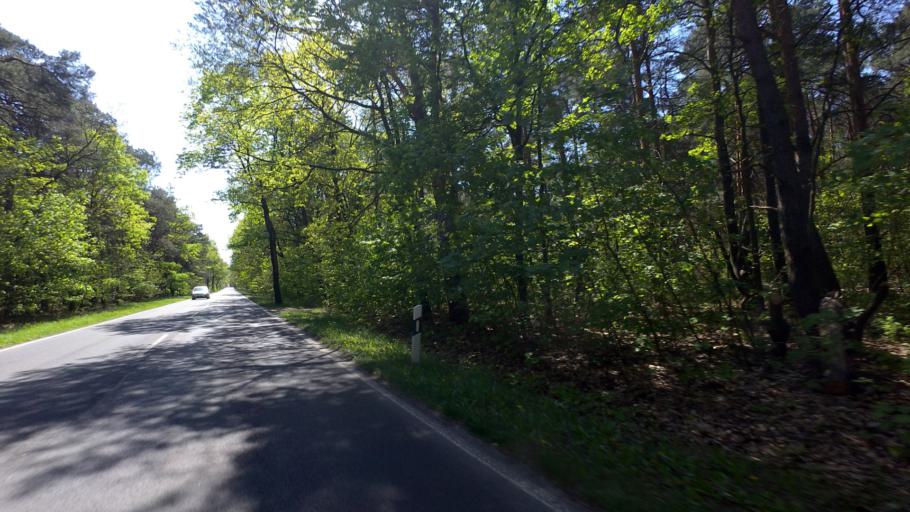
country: DE
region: Brandenburg
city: Bestensee
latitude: 52.2531
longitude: 13.6557
